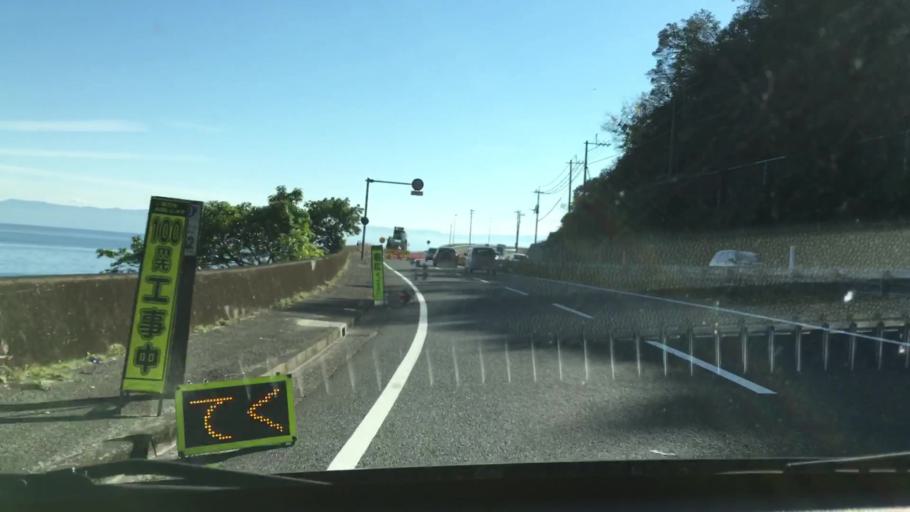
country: JP
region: Kagoshima
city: Kajiki
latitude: 31.6602
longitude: 130.6164
